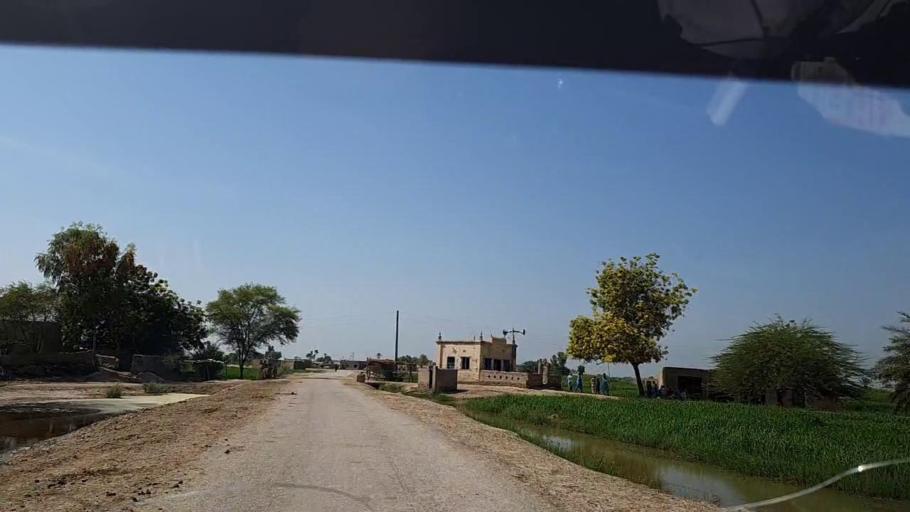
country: PK
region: Sindh
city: Tangwani
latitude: 28.3170
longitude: 69.0940
